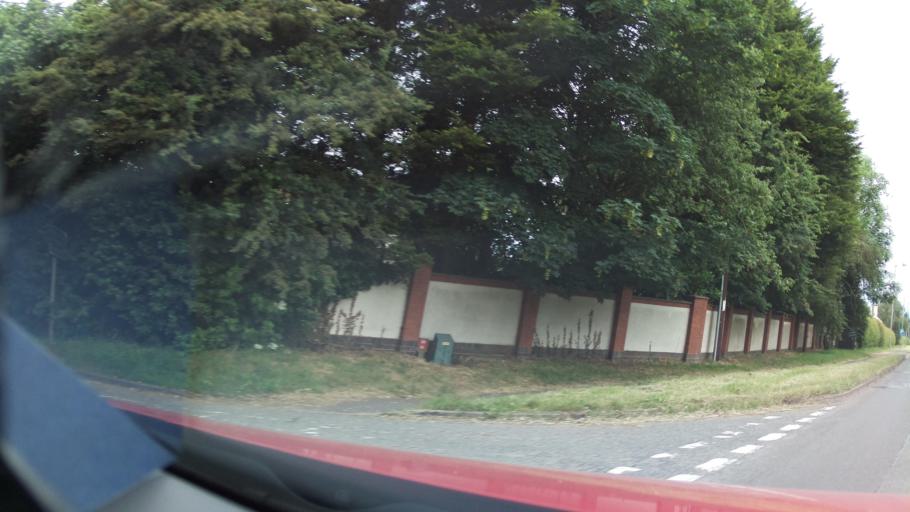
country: GB
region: England
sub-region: Staffordshire
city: Penkridge
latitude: 52.7139
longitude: -2.1214
